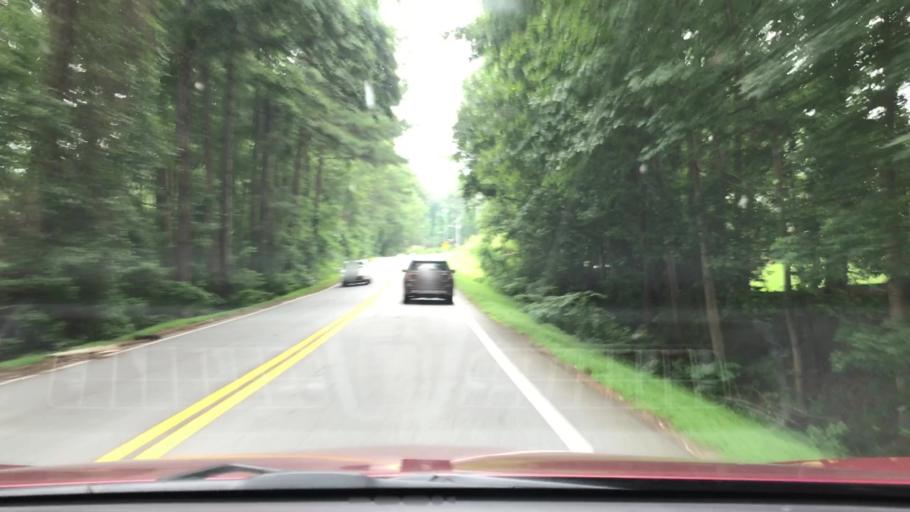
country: US
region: Georgia
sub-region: Gwinnett County
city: Suwanee
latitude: 34.0008
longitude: -84.0560
